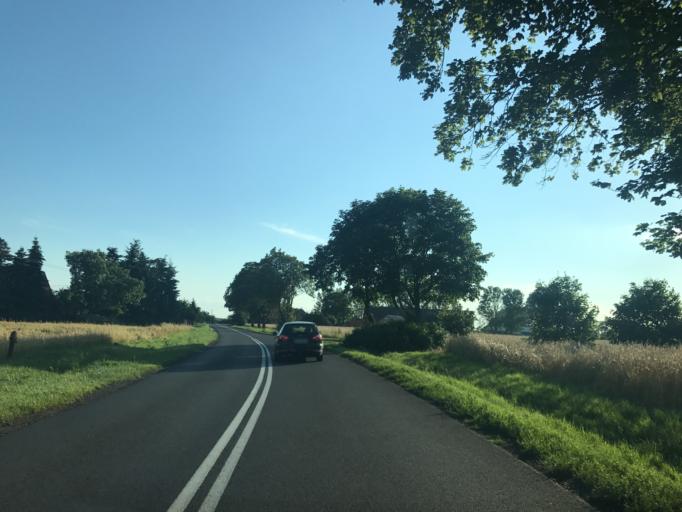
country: PL
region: Greater Poland Voivodeship
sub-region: Powiat koninski
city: Grodziec
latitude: 52.0467
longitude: 18.0945
